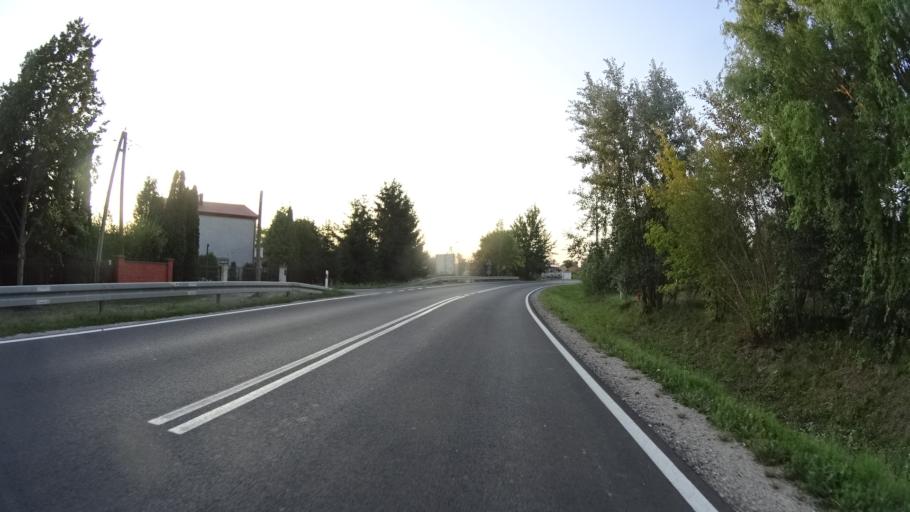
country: PL
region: Masovian Voivodeship
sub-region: Powiat warszawski zachodni
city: Truskaw
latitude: 52.2494
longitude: 20.7419
